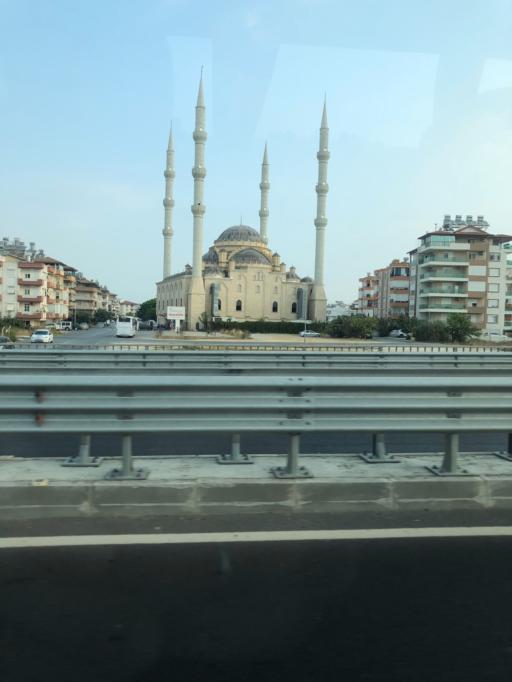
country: TR
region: Antalya
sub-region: Manavgat
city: Manavgat
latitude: 36.7765
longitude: 31.4539
